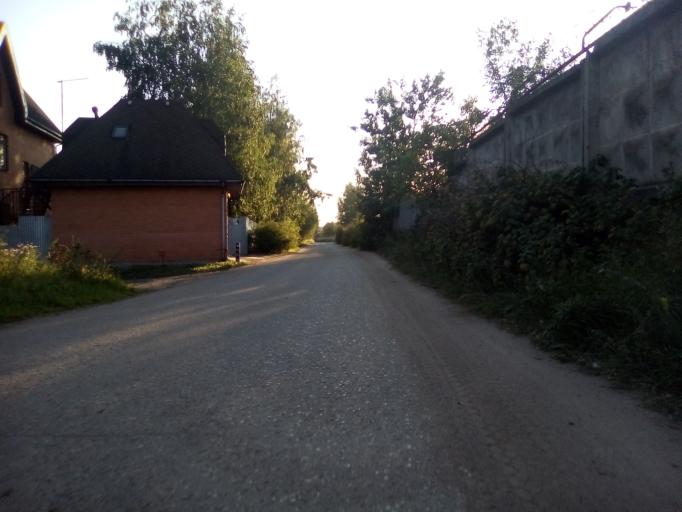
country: RU
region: Moskovskaya
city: Krasnoznamensk
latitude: 55.5807
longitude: 37.0432
